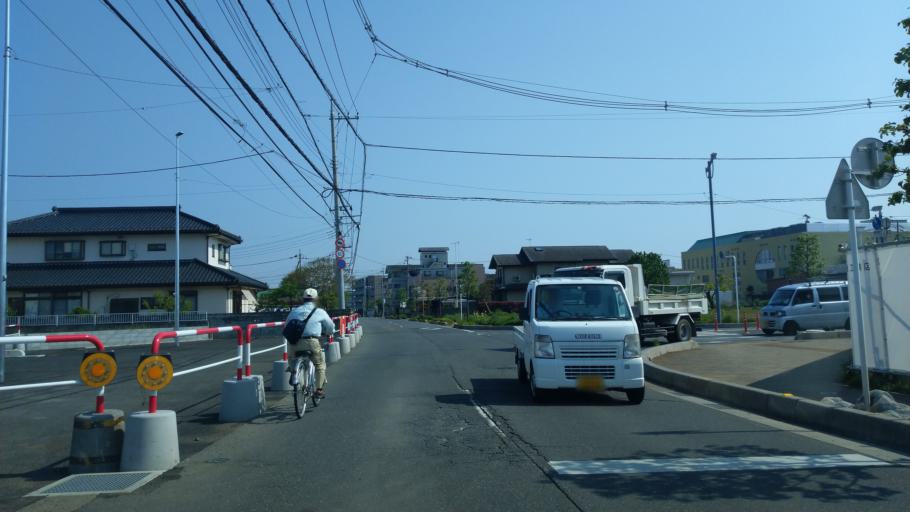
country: JP
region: Saitama
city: Kamifukuoka
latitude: 35.8660
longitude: 139.5296
